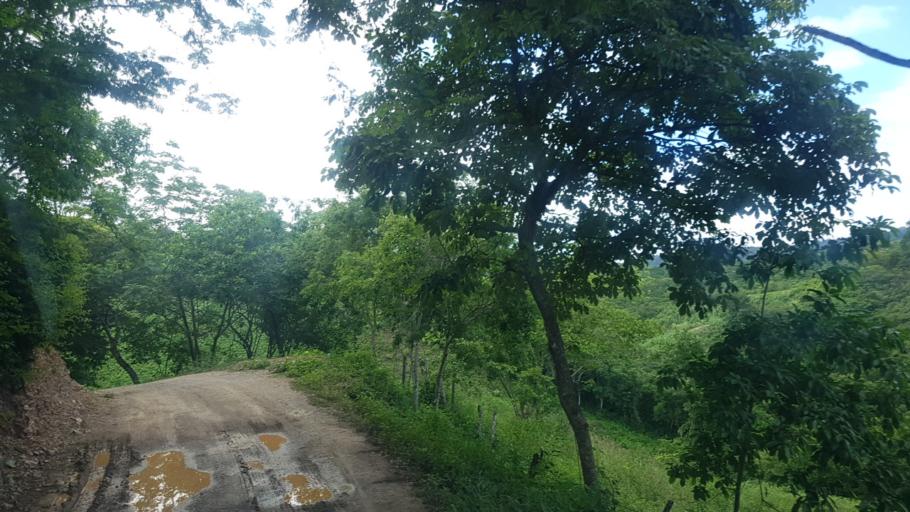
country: NI
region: Nueva Segovia
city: Ocotal
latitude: 13.5936
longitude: -86.4177
